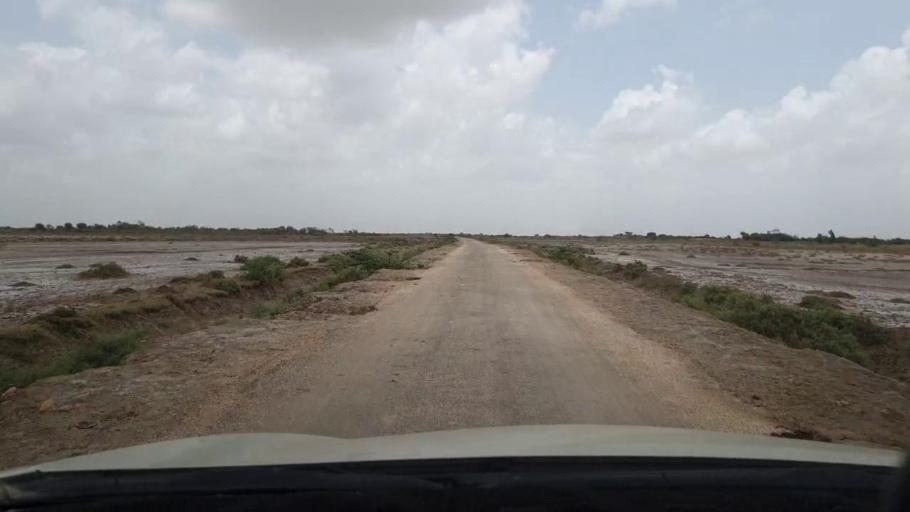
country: PK
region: Sindh
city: Kadhan
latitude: 24.3602
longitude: 68.9286
